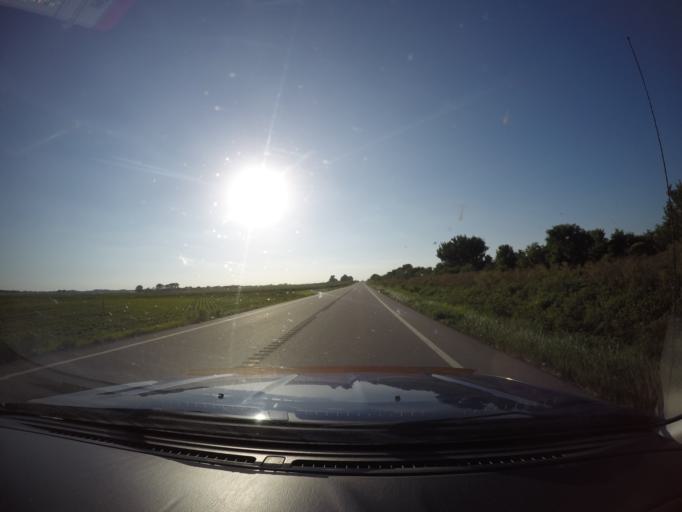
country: US
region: Kansas
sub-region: Shawnee County
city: Rossville
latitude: 39.1227
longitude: -95.9266
